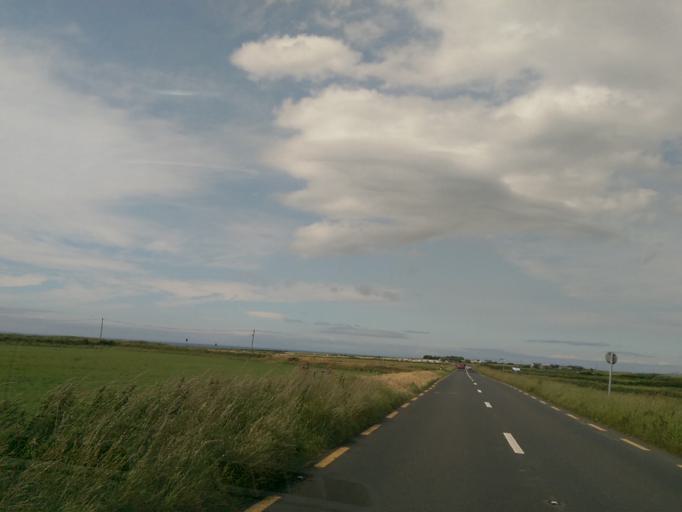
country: IE
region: Munster
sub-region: An Clar
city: Kilrush
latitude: 52.7991
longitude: -9.4473
